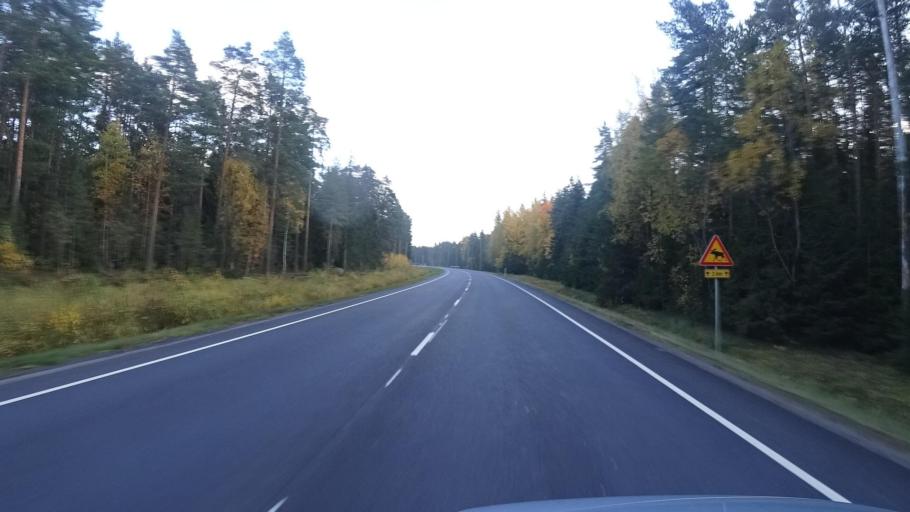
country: FI
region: Satakunta
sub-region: Rauma
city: Koeylioe
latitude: 61.0929
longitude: 22.2419
